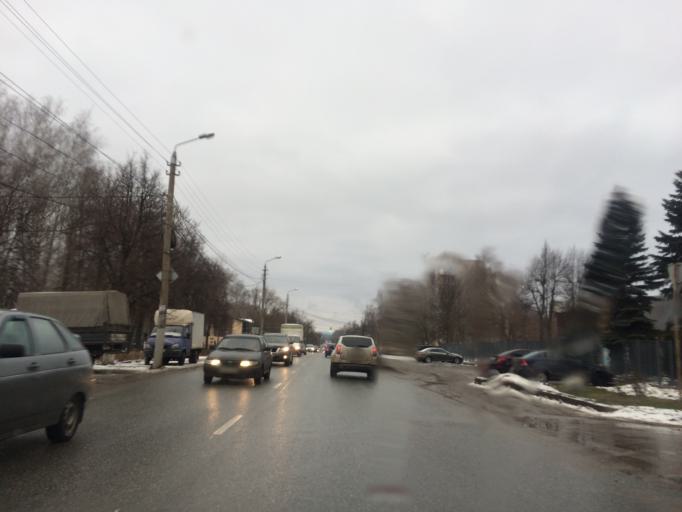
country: RU
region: Tula
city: Tula
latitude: 54.1951
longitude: 37.6912
